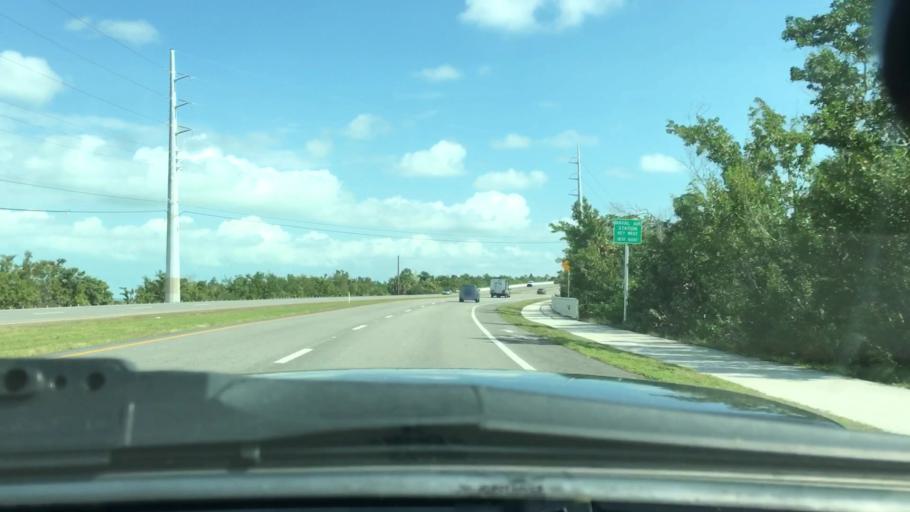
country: US
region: Florida
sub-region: Monroe County
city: Big Coppitt Key
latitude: 24.5870
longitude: -81.6956
